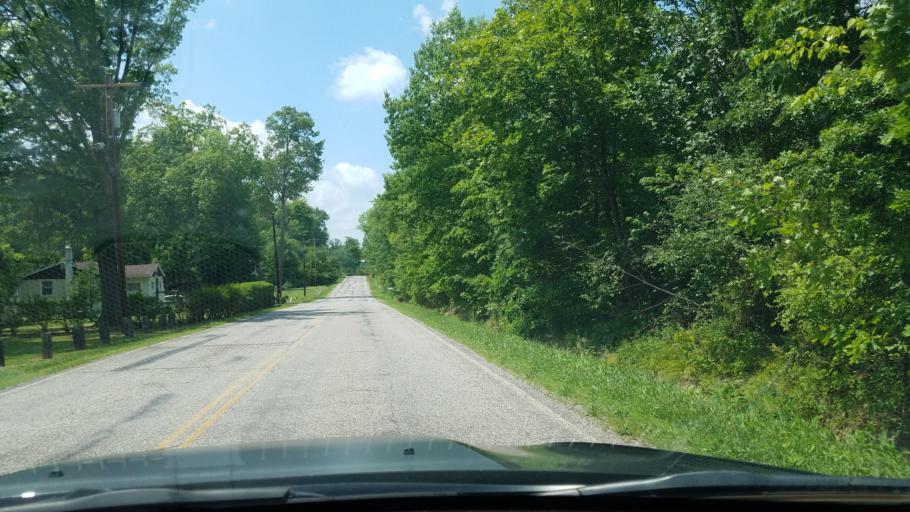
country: US
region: Ohio
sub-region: Trumbull County
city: Bolindale
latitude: 41.2033
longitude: -80.7918
